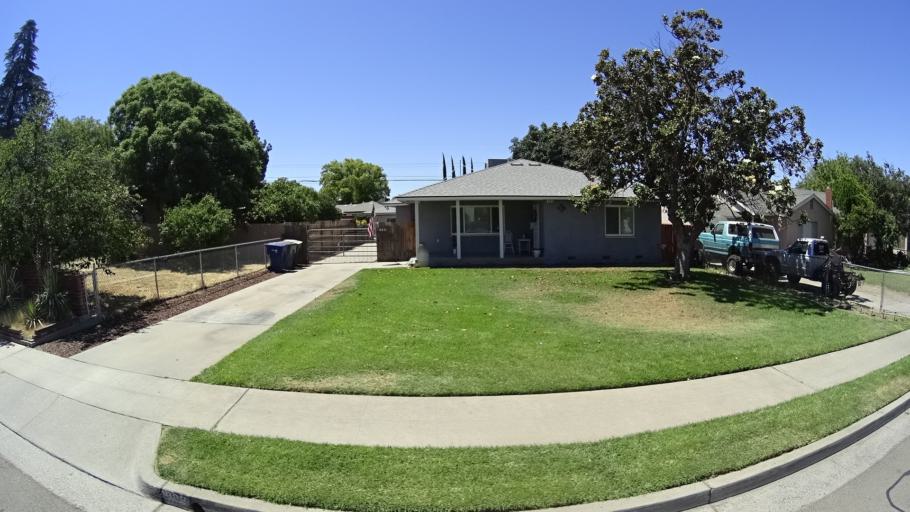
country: US
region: California
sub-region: Fresno County
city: Fresno
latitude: 36.7720
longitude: -119.8228
